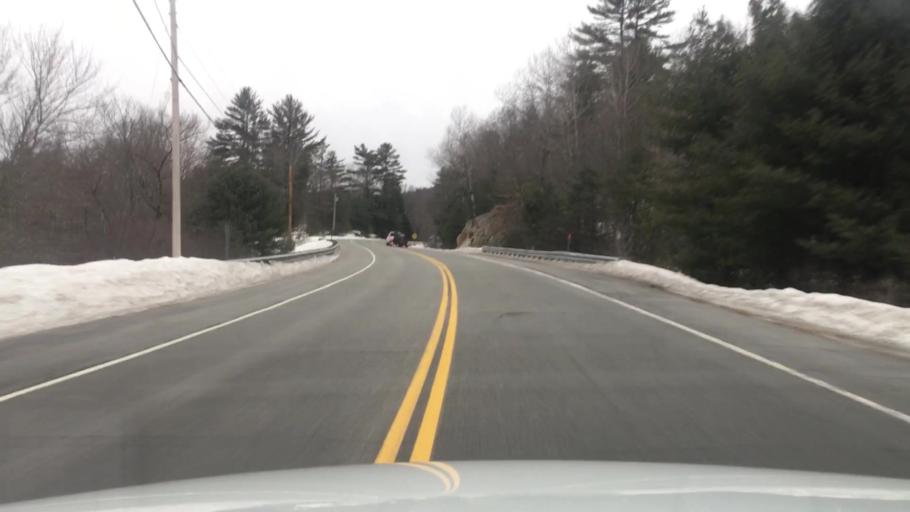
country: US
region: Maine
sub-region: York County
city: Limerick
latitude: 43.7275
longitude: -70.8141
